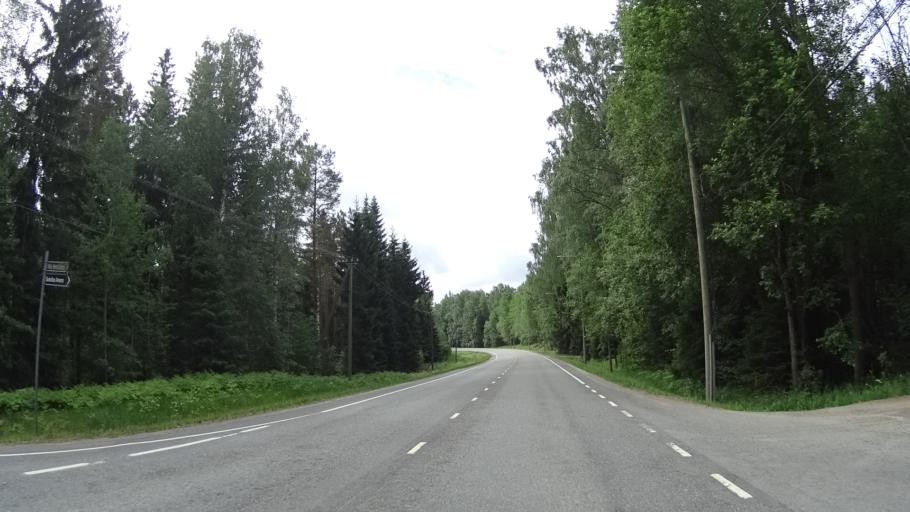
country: FI
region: Uusimaa
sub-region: Helsinki
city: Vihti
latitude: 60.2830
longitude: 24.4085
